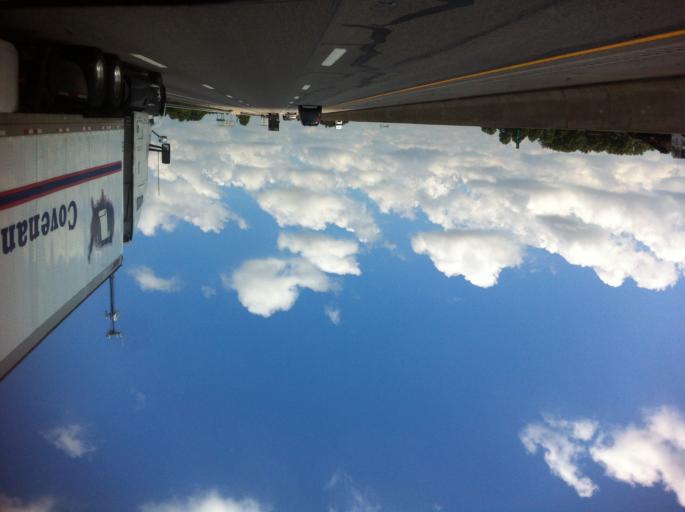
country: US
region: Ohio
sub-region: Huron County
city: Monroeville
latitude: 41.3357
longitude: -82.6919
